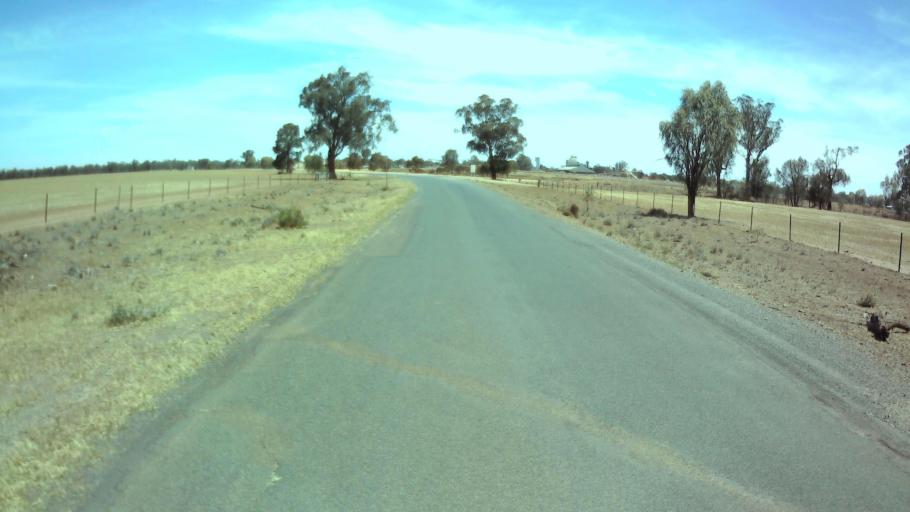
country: AU
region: New South Wales
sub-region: Weddin
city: Grenfell
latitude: -33.8304
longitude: 147.7458
